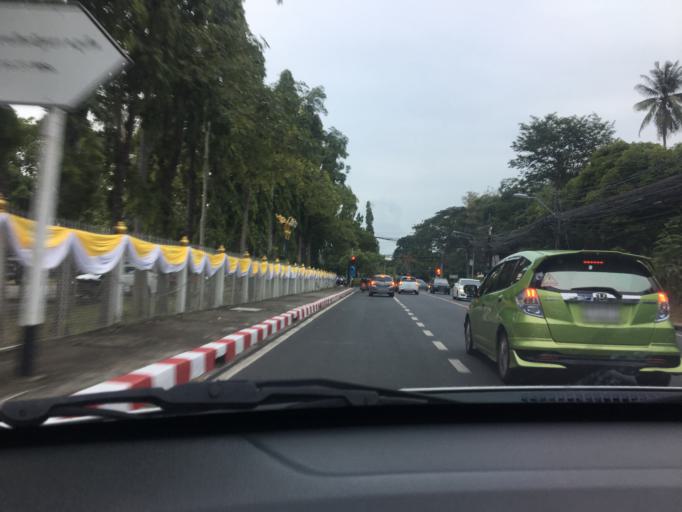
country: TH
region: Phuket
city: Phuket
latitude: 7.8905
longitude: 98.3984
